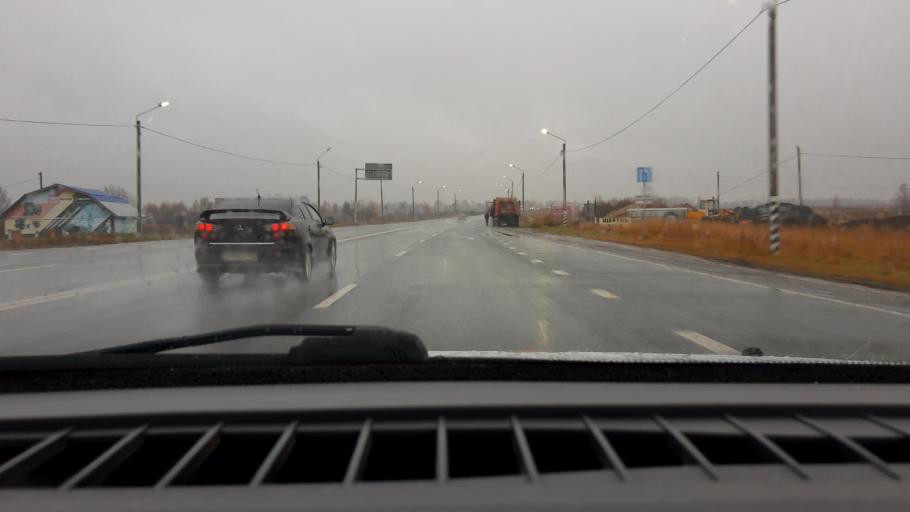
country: RU
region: Nizjnij Novgorod
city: Sitniki
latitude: 56.5011
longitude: 44.0251
